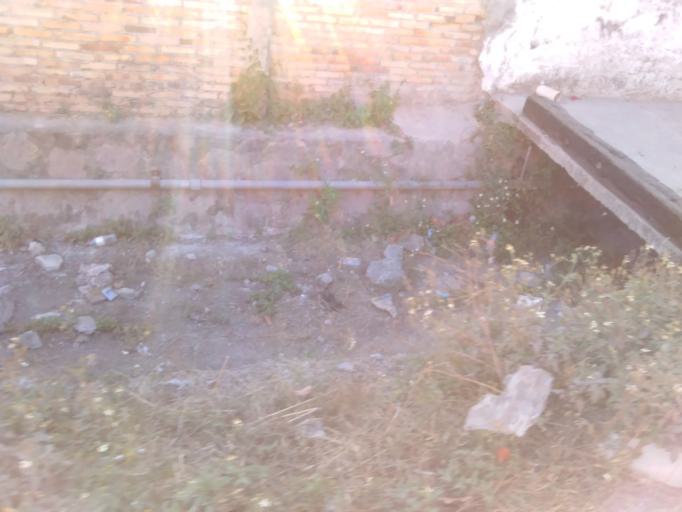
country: MX
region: Nayarit
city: Tepic
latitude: 21.5060
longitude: -104.8830
